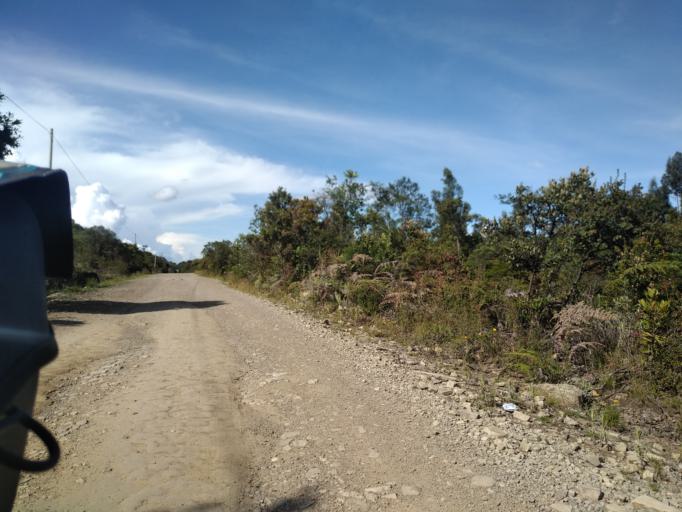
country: CO
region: Cundinamarca
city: Guacheta
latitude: 5.4529
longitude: -73.6498
